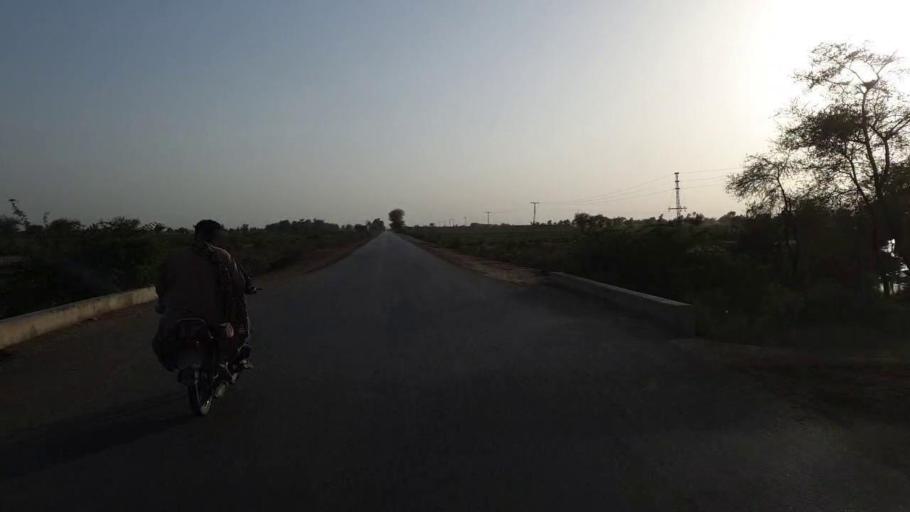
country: PK
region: Sindh
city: Jam Sahib
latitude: 26.2879
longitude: 68.6008
